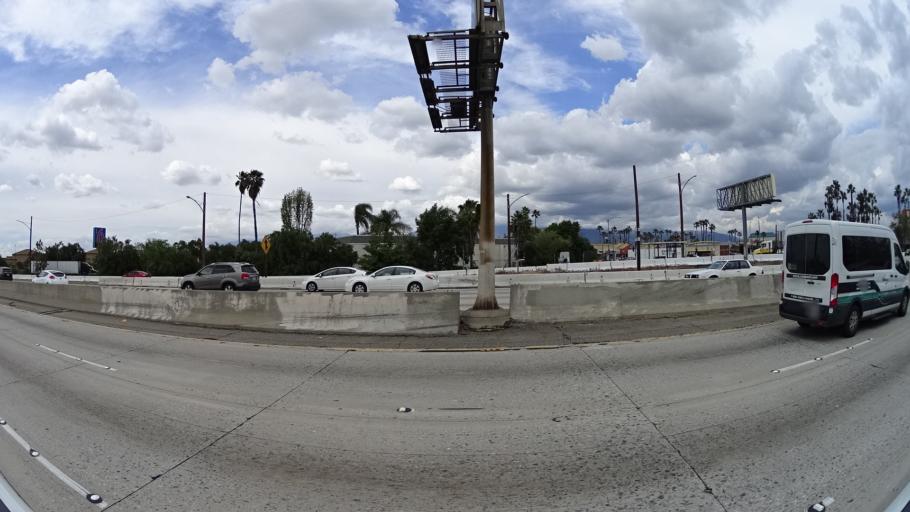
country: US
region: California
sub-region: Los Angeles County
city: Baldwin Park
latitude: 34.0702
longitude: -117.9604
